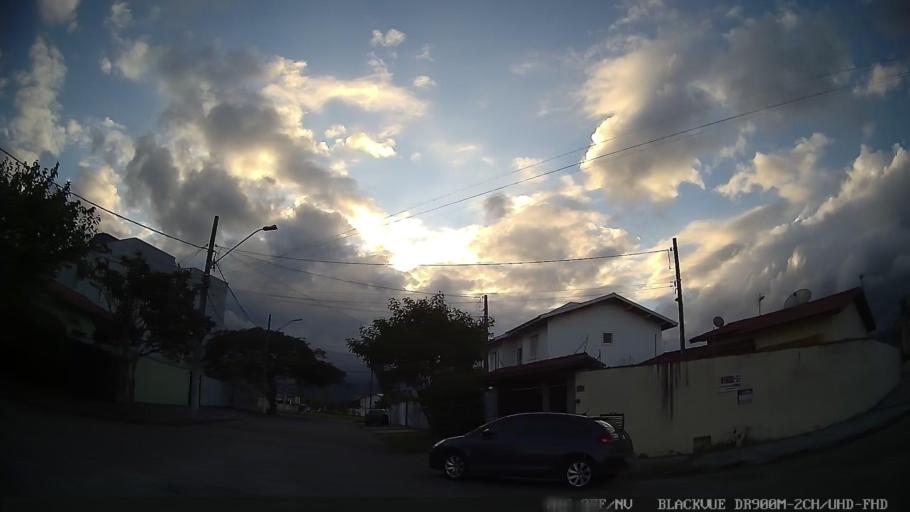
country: BR
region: Sao Paulo
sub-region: Caraguatatuba
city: Caraguatatuba
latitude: -23.6636
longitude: -45.4460
